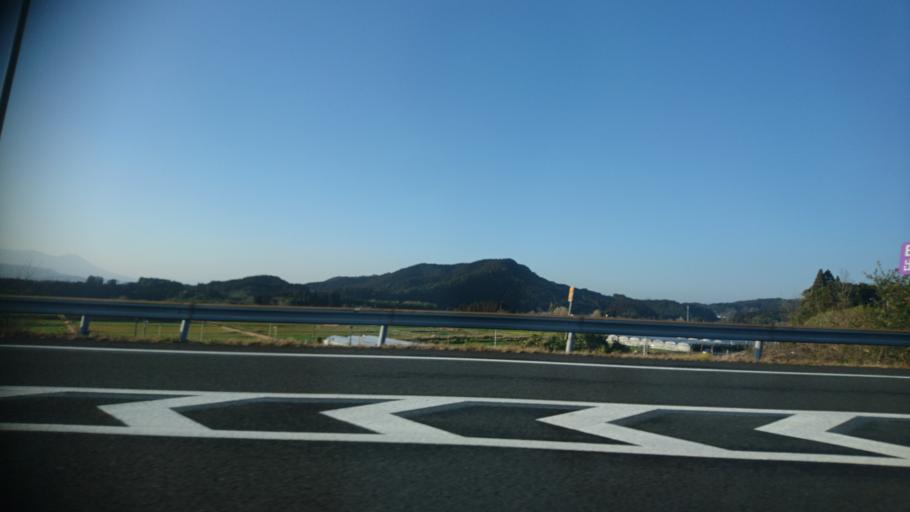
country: JP
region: Miyazaki
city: Miyakonojo
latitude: 31.7947
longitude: 131.1617
